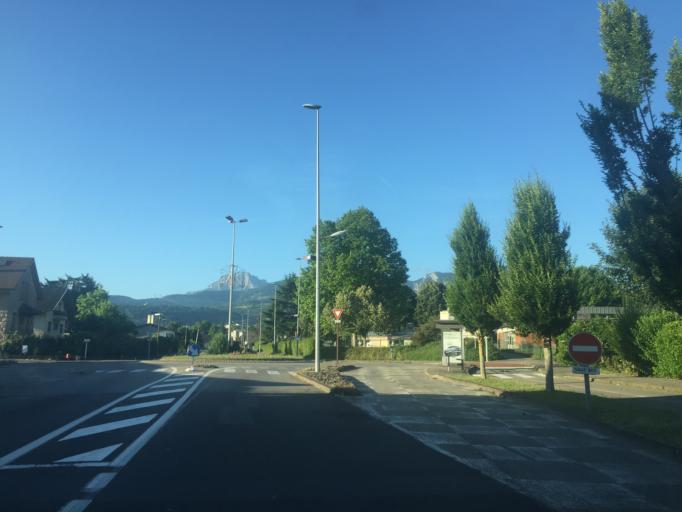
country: FR
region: Rhone-Alpes
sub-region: Departement de la Savoie
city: Cognin
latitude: 45.5693
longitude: 5.8922
